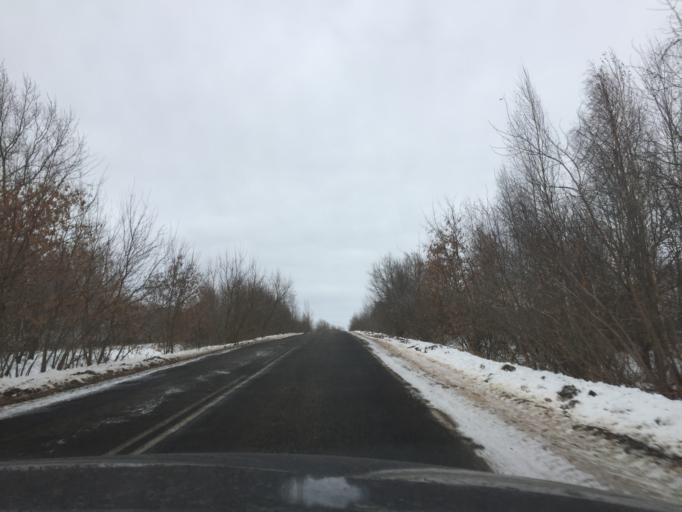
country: RU
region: Tula
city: Shchekino
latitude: 53.8206
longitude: 37.5264
